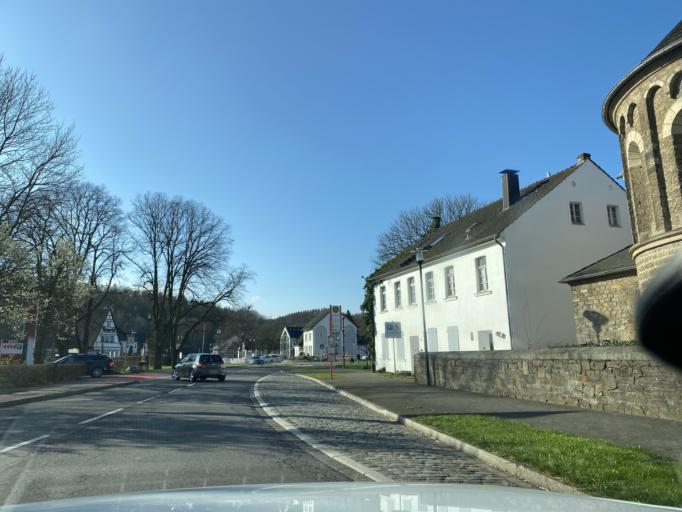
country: DE
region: North Rhine-Westphalia
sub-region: Regierungsbezirk Koln
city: Odenthal
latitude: 51.0336
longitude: 7.1175
